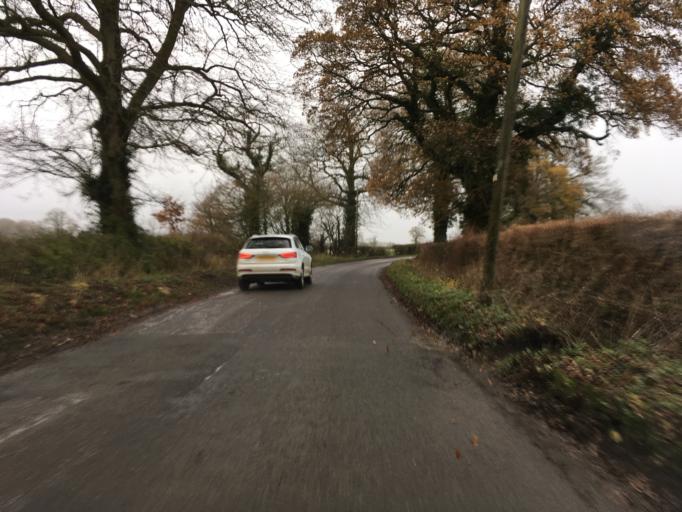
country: GB
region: England
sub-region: Wiltshire
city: Luckington
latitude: 51.5256
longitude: -2.2101
